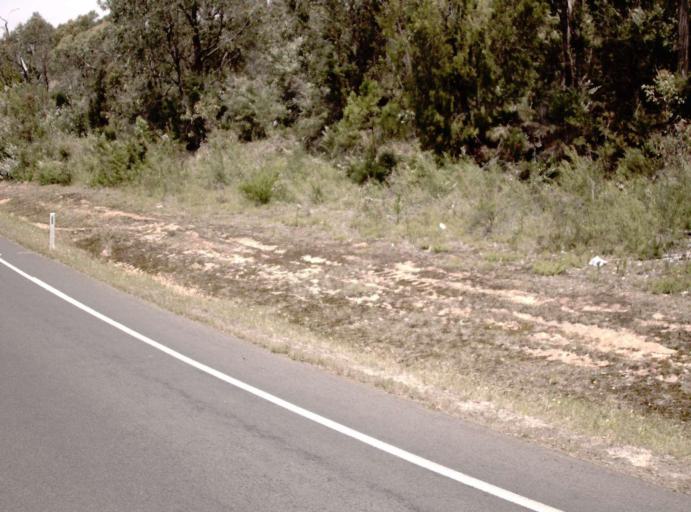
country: AU
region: Victoria
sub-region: Latrobe
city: Traralgon
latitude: -38.2776
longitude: 146.6939
